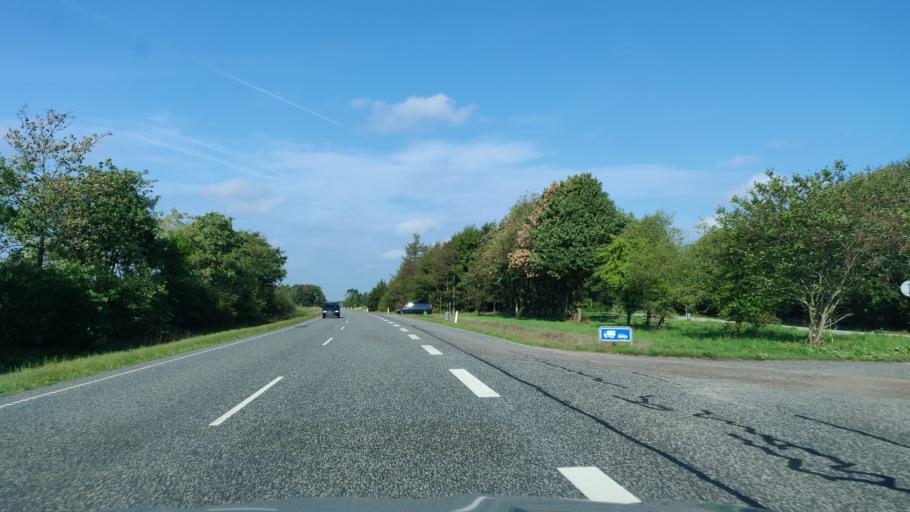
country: DK
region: Central Jutland
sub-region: Herning Kommune
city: Sunds
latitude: 56.2437
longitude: 9.0822
